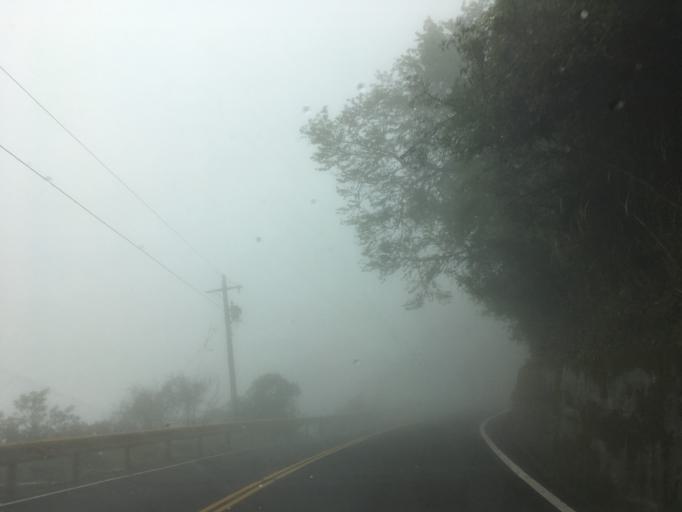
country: TW
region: Taiwan
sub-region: Hualien
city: Hualian
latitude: 24.1971
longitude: 121.4309
